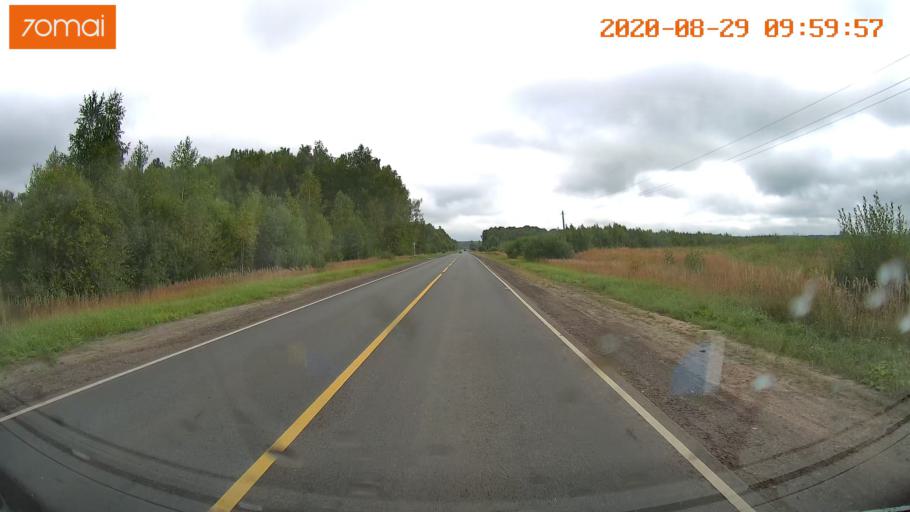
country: RU
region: Ivanovo
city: Zarechnyy
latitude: 57.4103
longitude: 42.3801
